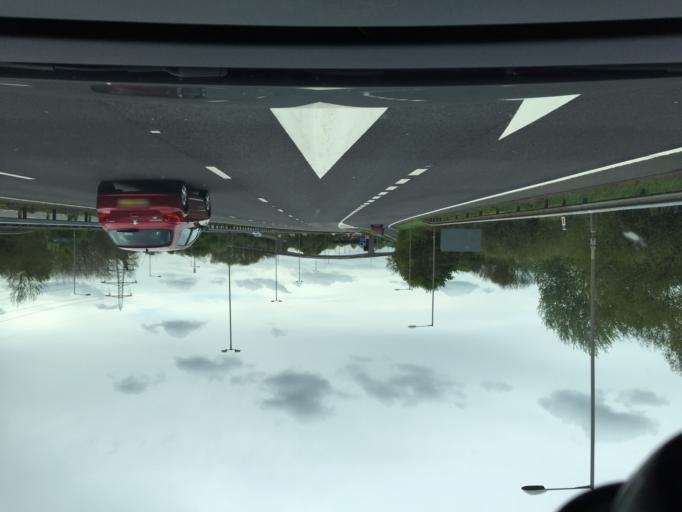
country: GB
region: England
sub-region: West Berkshire
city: Theale
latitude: 51.4425
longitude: -1.0703
